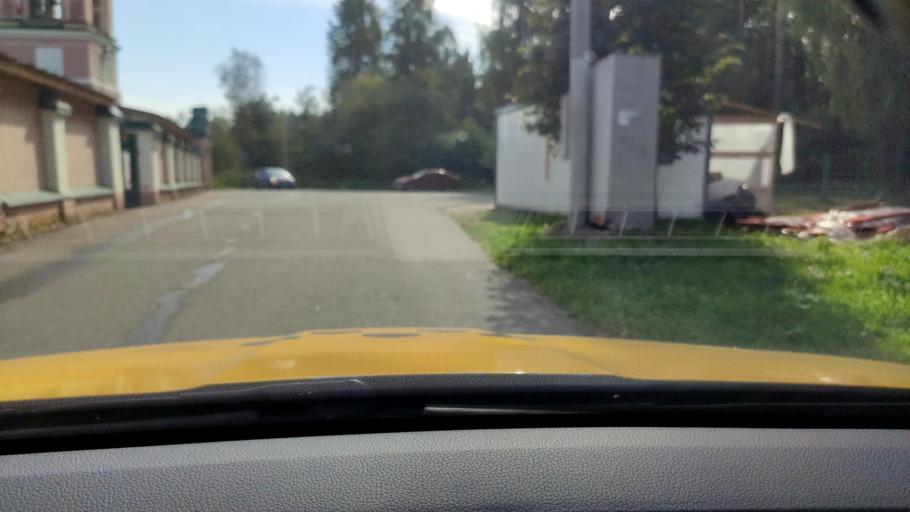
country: RU
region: Moskovskaya
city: Shcherbinka
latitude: 55.4964
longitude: 37.5869
